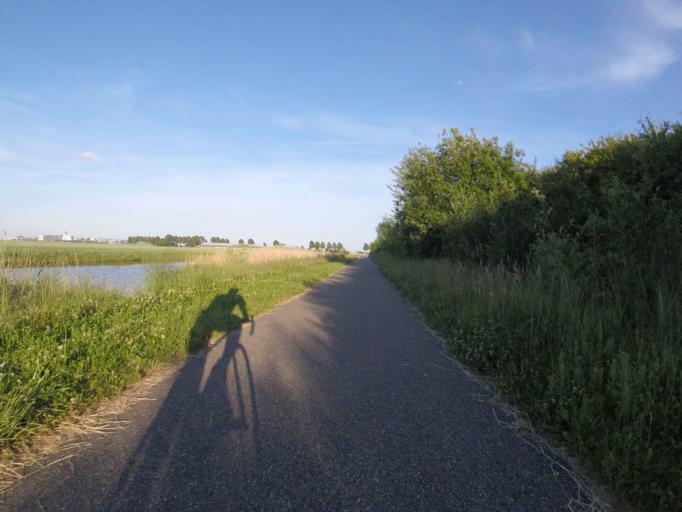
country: NL
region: North Holland
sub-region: Gemeente Haarlemmermeer
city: Hoofddorp
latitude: 52.3049
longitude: 4.7185
